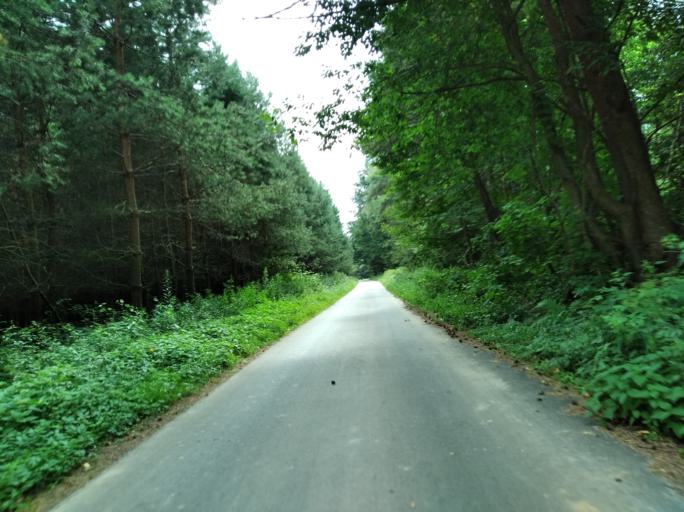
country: PL
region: Subcarpathian Voivodeship
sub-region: Powiat krosnienski
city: Odrzykon
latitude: 49.7824
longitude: 21.7196
